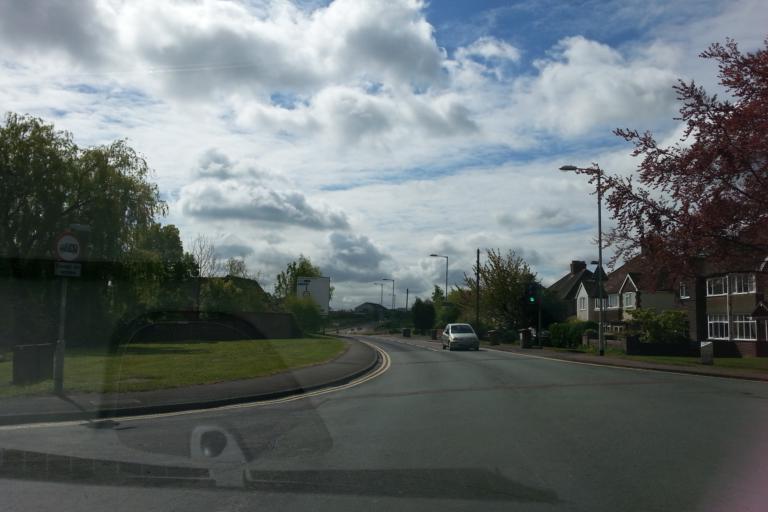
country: GB
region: England
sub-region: Staffordshire
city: Lichfield
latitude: 52.6712
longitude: -1.8322
